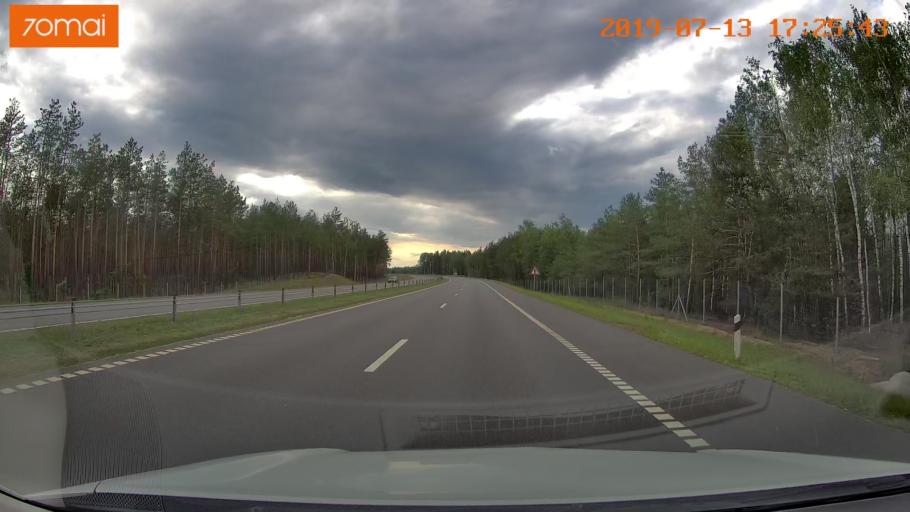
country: BY
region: Mogilev
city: Babruysk
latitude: 53.2557
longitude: 29.2021
